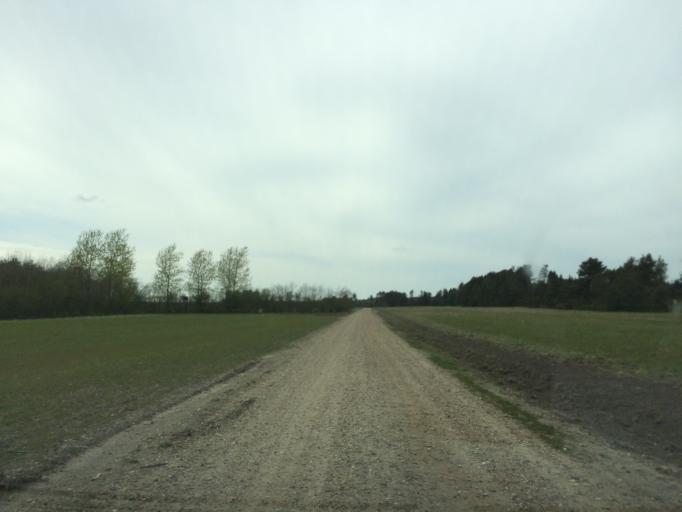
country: DK
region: Central Jutland
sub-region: Holstebro Kommune
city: Ulfborg
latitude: 56.2449
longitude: 8.4441
